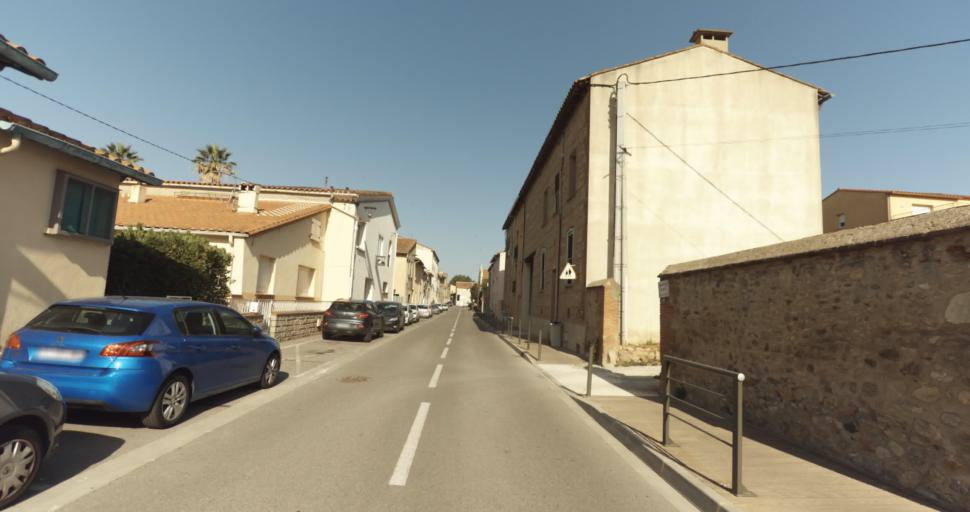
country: FR
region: Languedoc-Roussillon
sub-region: Departement des Pyrenees-Orientales
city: Alenya
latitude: 42.6387
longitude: 2.9837
